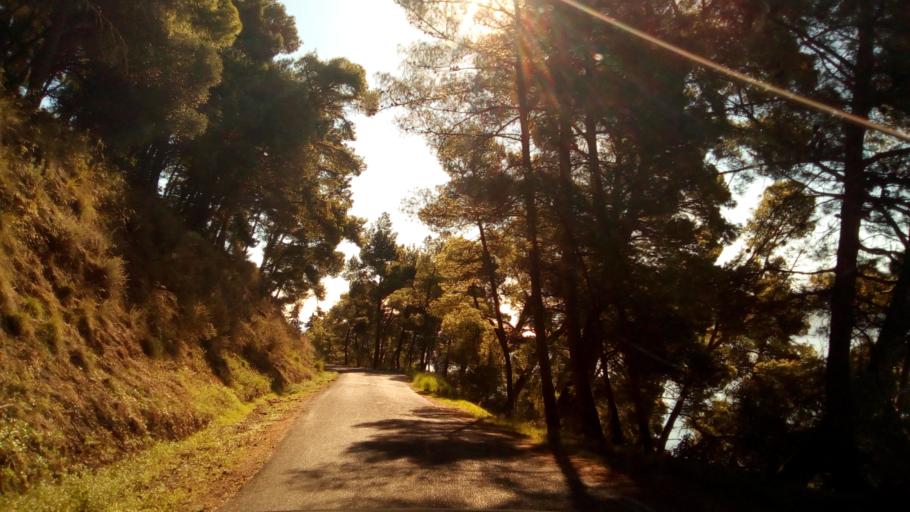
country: GR
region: West Greece
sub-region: Nomos Aitolias kai Akarnanias
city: Nafpaktos
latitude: 38.3952
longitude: 21.8239
